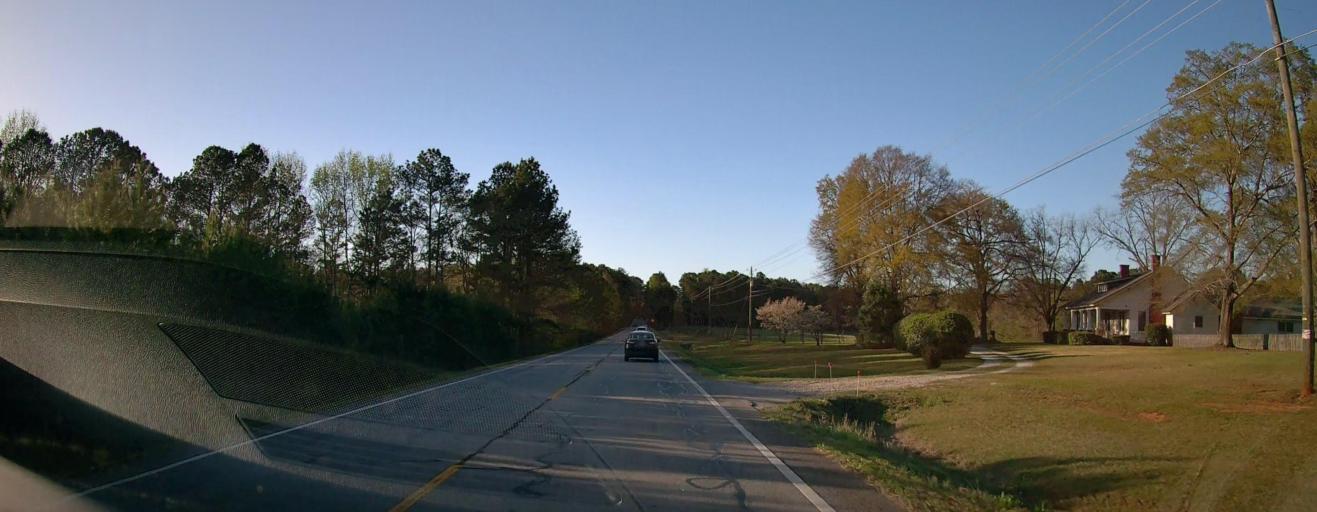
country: US
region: Georgia
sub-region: Newton County
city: Oakwood
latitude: 33.5055
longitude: -83.9213
